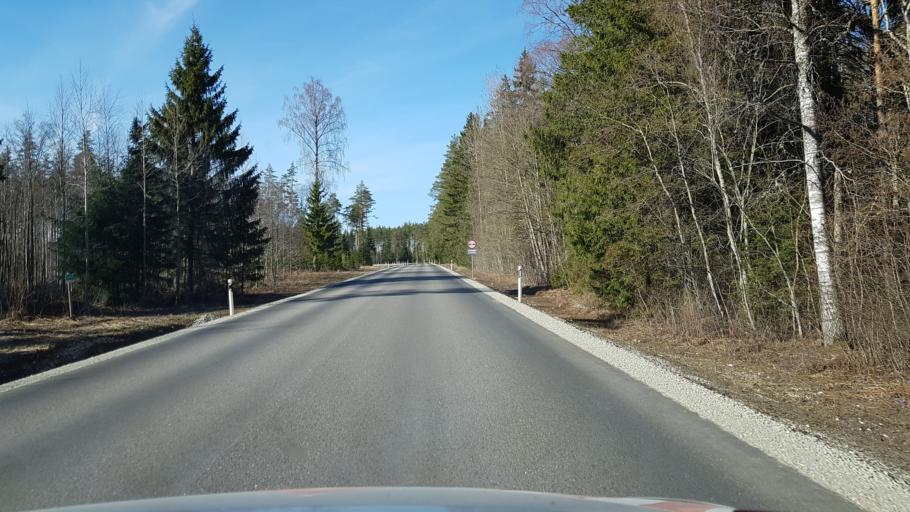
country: EE
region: Laeaene-Virumaa
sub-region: Vinni vald
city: Vinni
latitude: 59.1217
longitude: 26.6174
